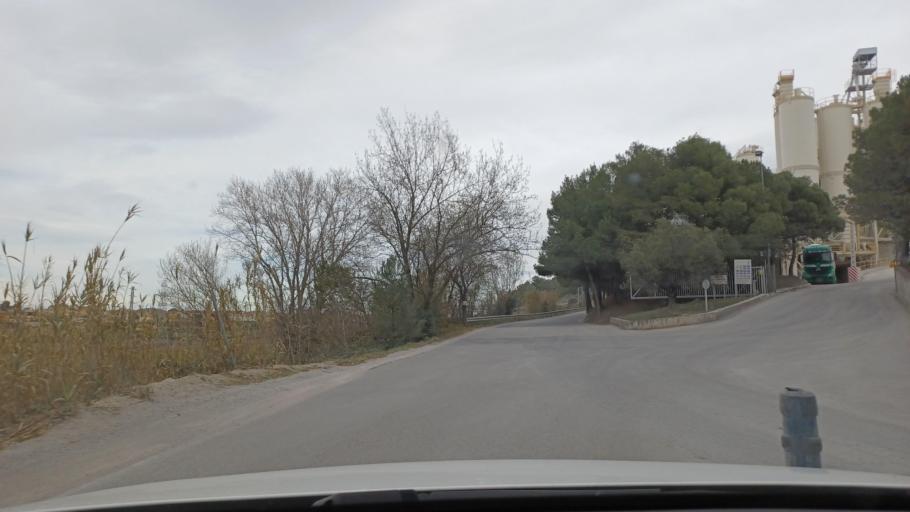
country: ES
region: Catalonia
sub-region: Provincia de Barcelona
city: Vilafranca del Penedes
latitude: 41.3649
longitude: 1.6818
